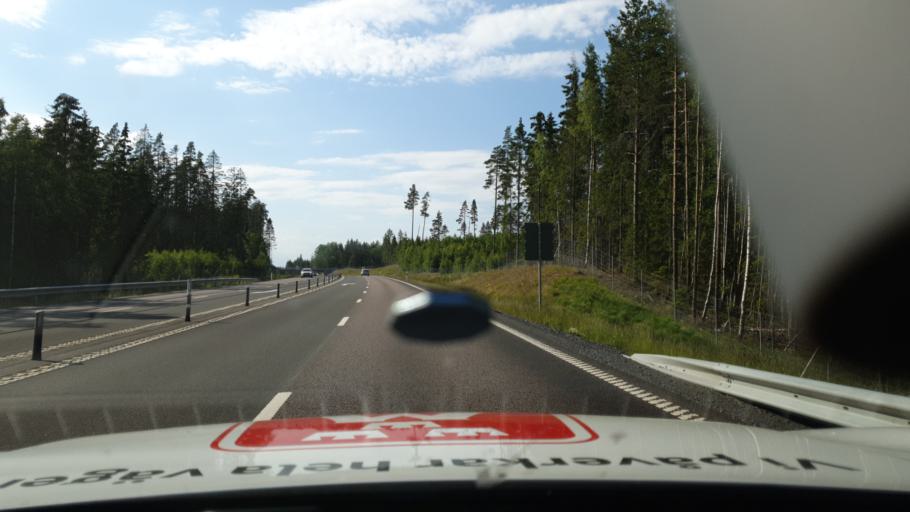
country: SE
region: Joenkoeping
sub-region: Mullsjo Kommun
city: Mullsjoe
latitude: 57.8913
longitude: 13.8875
